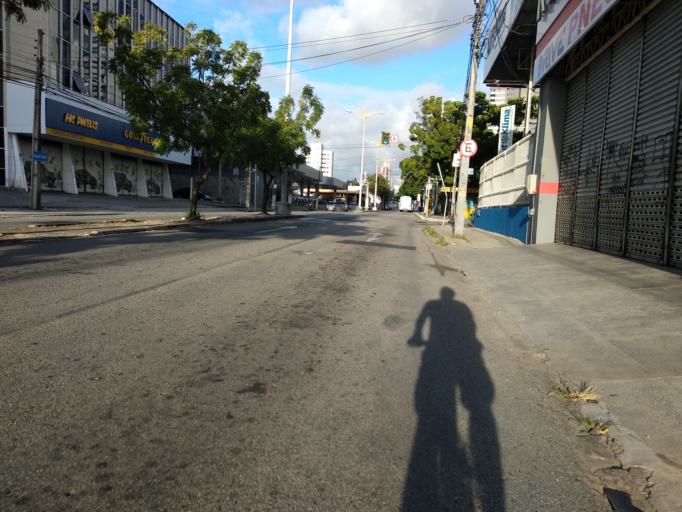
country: BR
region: Ceara
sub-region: Fortaleza
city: Fortaleza
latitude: -3.7366
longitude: -38.5150
